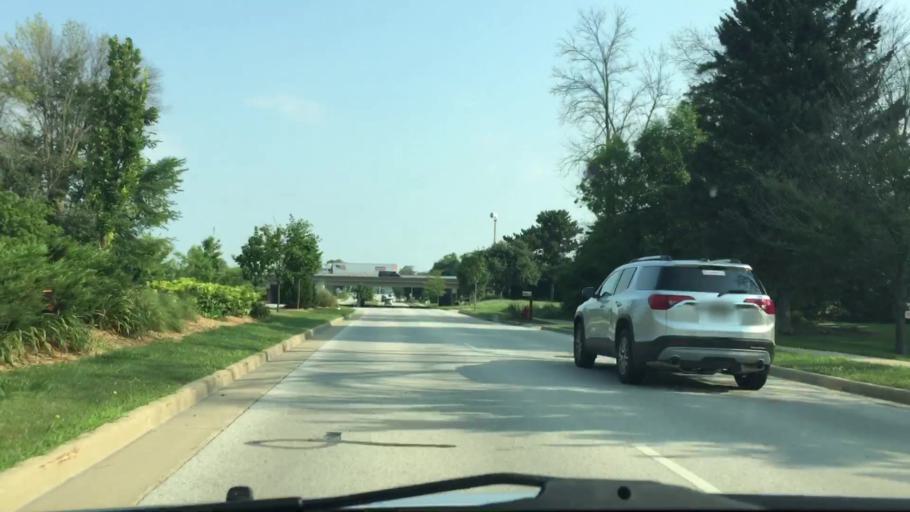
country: US
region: Wisconsin
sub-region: Waukesha County
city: Brookfield
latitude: 43.0262
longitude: -88.1269
